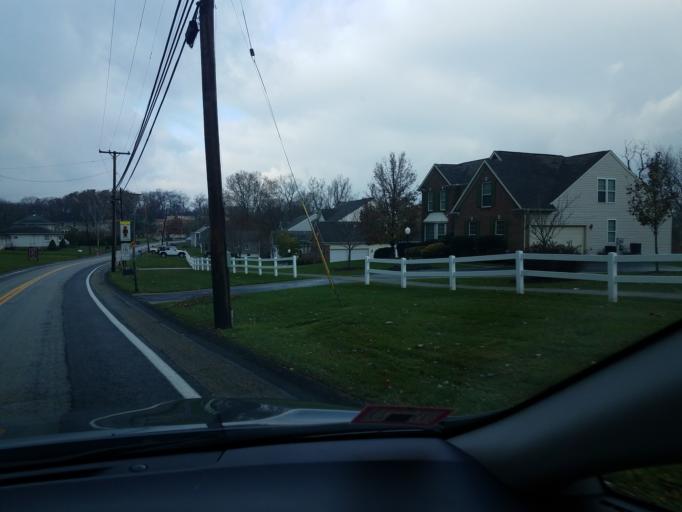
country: US
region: Pennsylvania
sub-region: Allegheny County
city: Franklin Park
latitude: 40.5860
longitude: -80.0923
